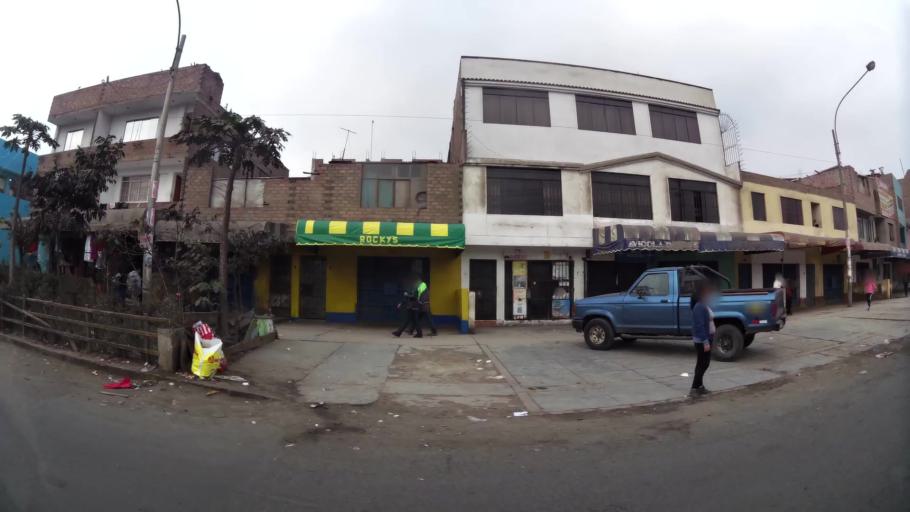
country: PE
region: Lima
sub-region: Lima
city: Independencia
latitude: -11.9985
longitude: -77.0004
